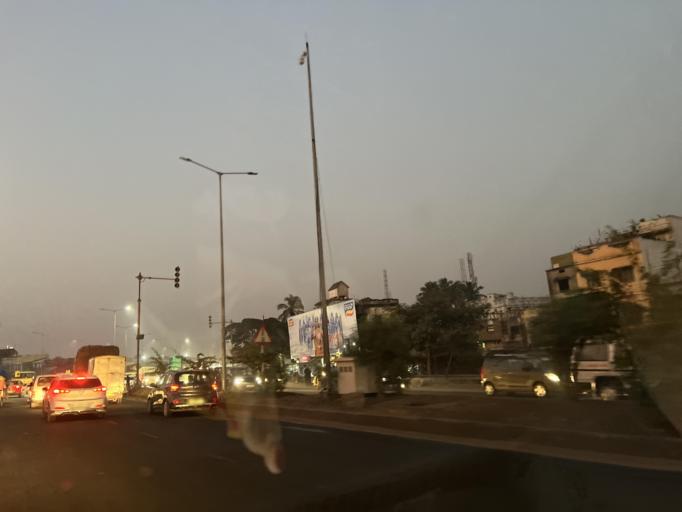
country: IN
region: Odisha
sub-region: Cuttack
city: Cuttack
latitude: 20.4279
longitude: 85.8775
